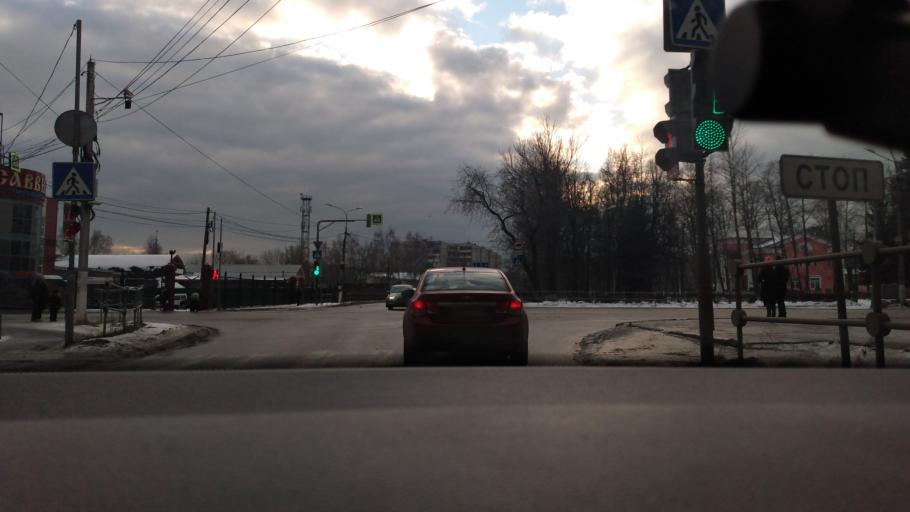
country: RU
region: Moskovskaya
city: Zheleznodorozhnyy
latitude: 55.7302
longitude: 38.0295
